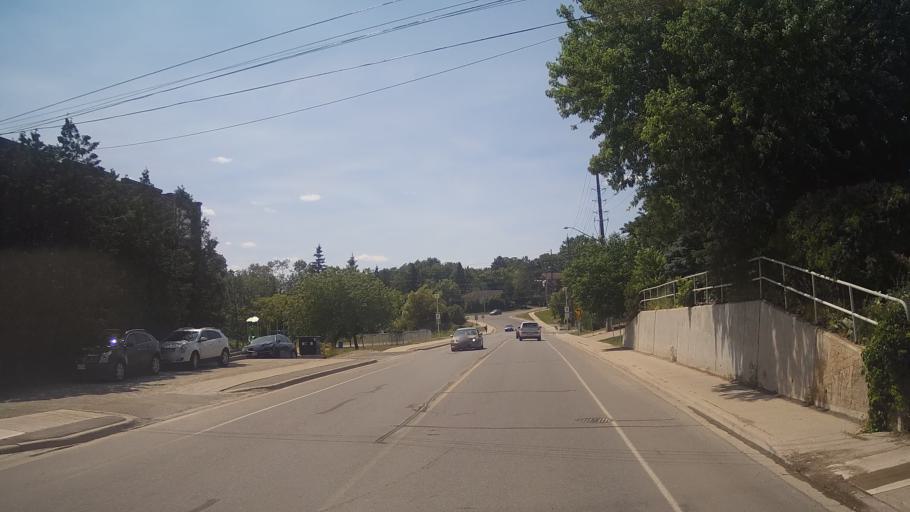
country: CA
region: Ontario
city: Greater Sudbury
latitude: 46.4611
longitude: -81.0122
